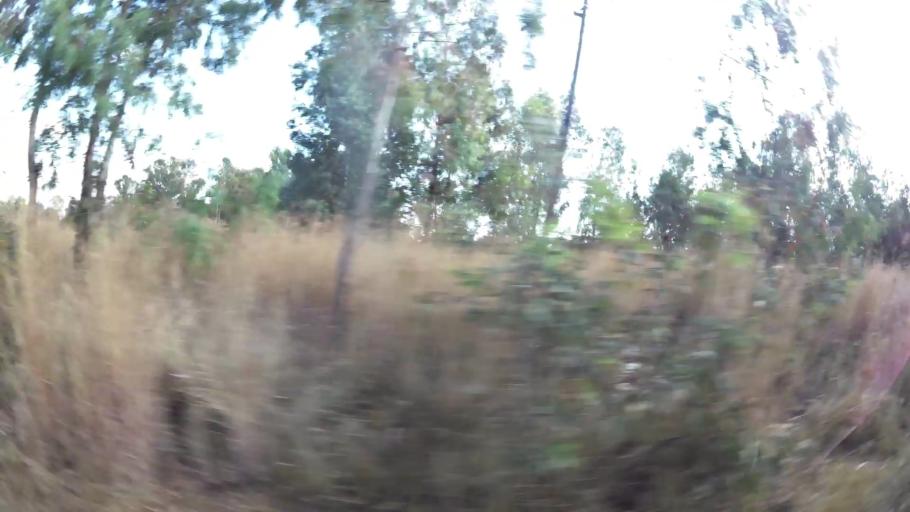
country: ZA
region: Gauteng
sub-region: Ekurhuleni Metropolitan Municipality
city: Benoni
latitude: -26.0934
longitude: 28.3612
